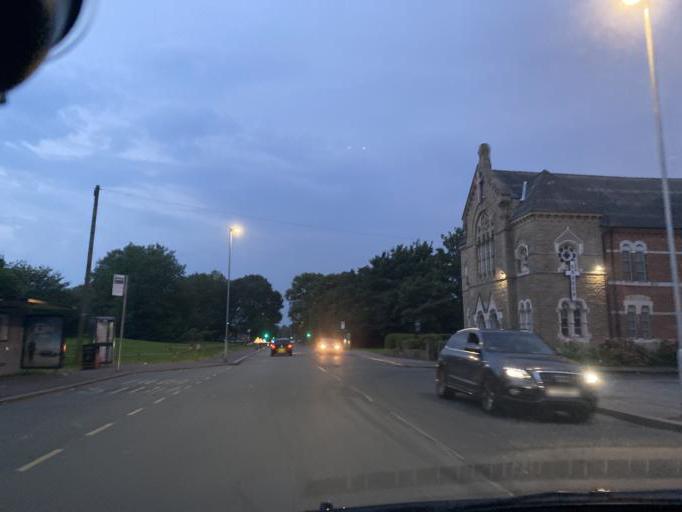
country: GB
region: England
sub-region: Manchester
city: Hulme
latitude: 53.4617
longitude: -2.2580
